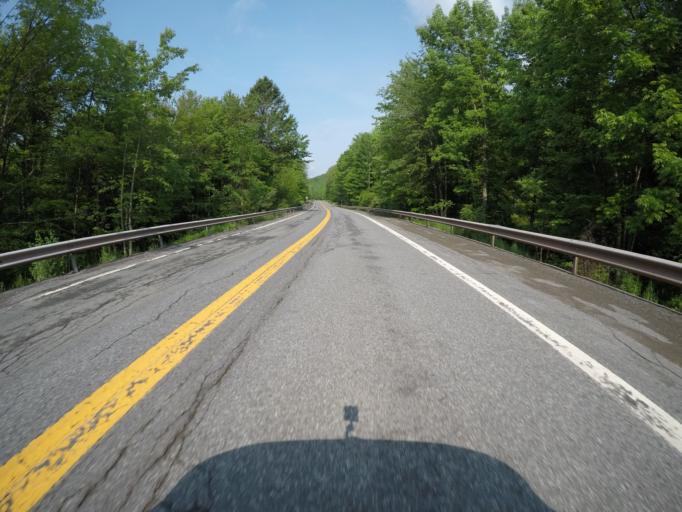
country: US
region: New York
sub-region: Delaware County
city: Delhi
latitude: 42.1194
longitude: -74.7495
